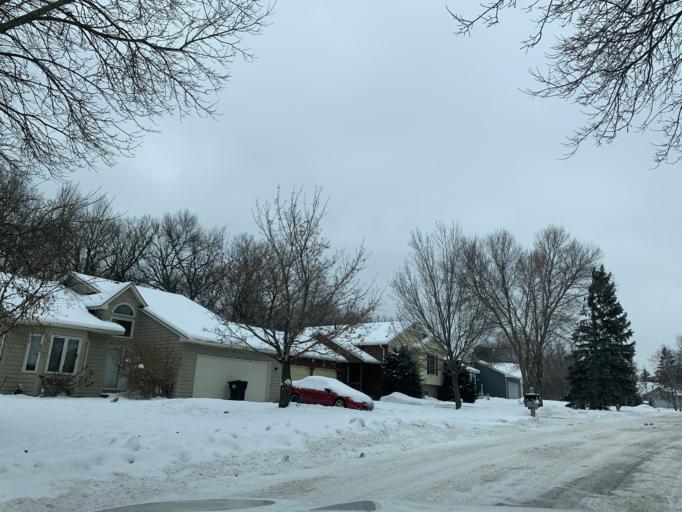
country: US
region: Minnesota
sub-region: Anoka County
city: Coon Rapids
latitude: 45.1594
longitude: -93.2987
